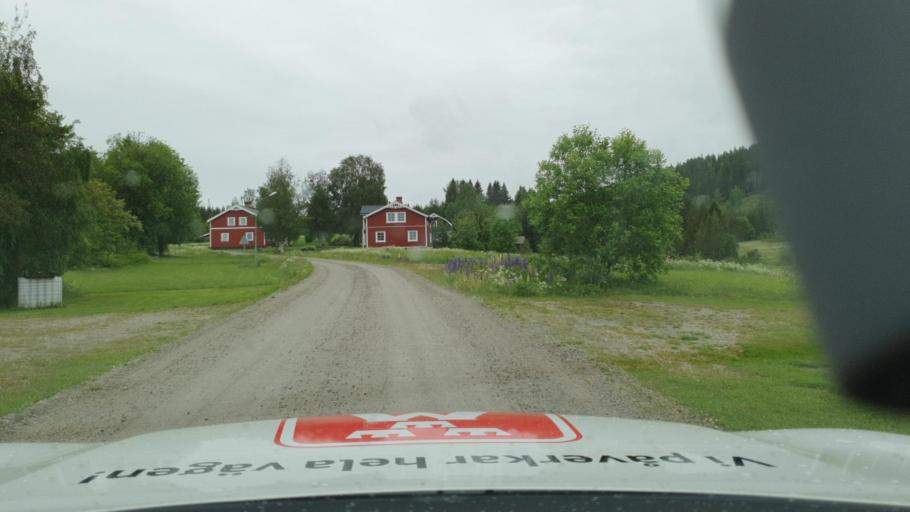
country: SE
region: Vaesterbotten
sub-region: Asele Kommun
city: Asele
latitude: 63.9664
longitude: 17.1041
